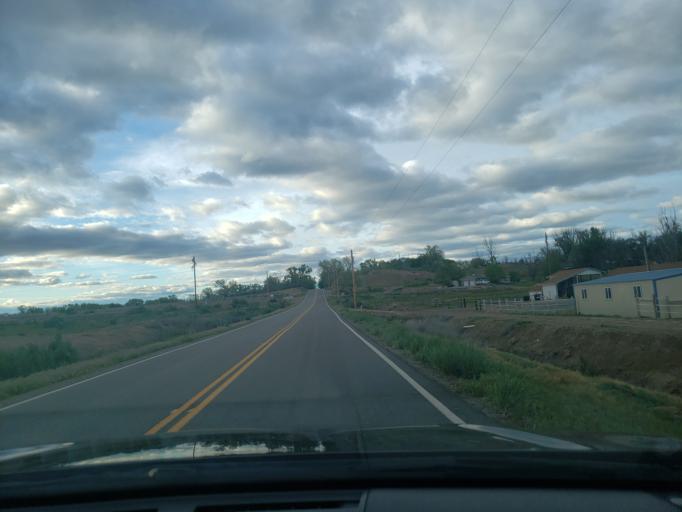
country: US
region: Colorado
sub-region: Mesa County
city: Fruita
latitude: 39.1881
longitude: -108.7291
